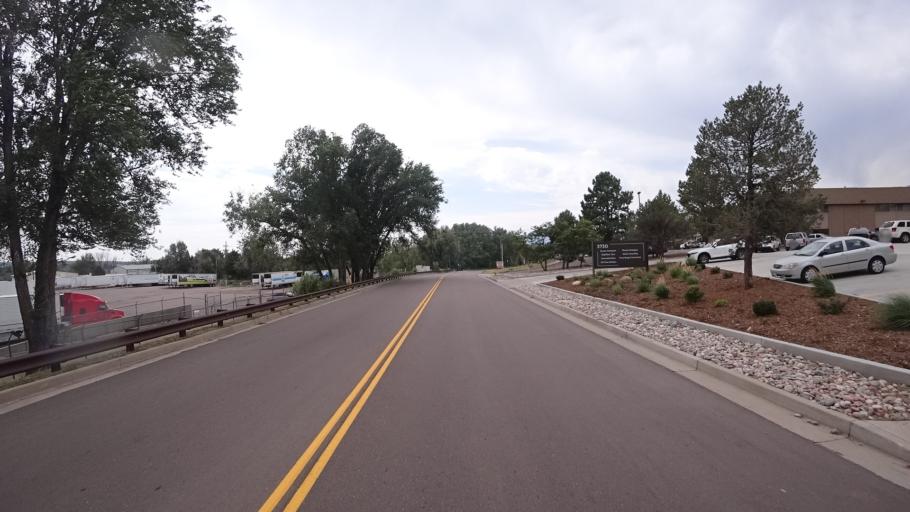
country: US
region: Colorado
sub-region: El Paso County
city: Colorado Springs
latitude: 38.8858
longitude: -104.8340
